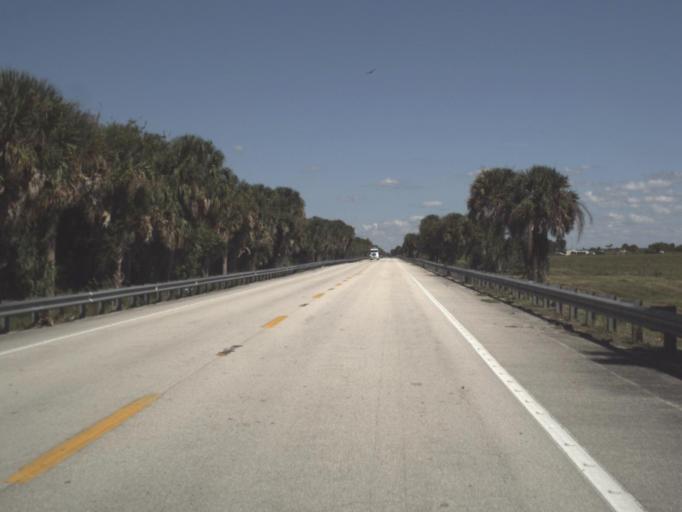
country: US
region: Florida
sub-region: Glades County
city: Buckhead Ridge
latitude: 27.0851
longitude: -80.9665
